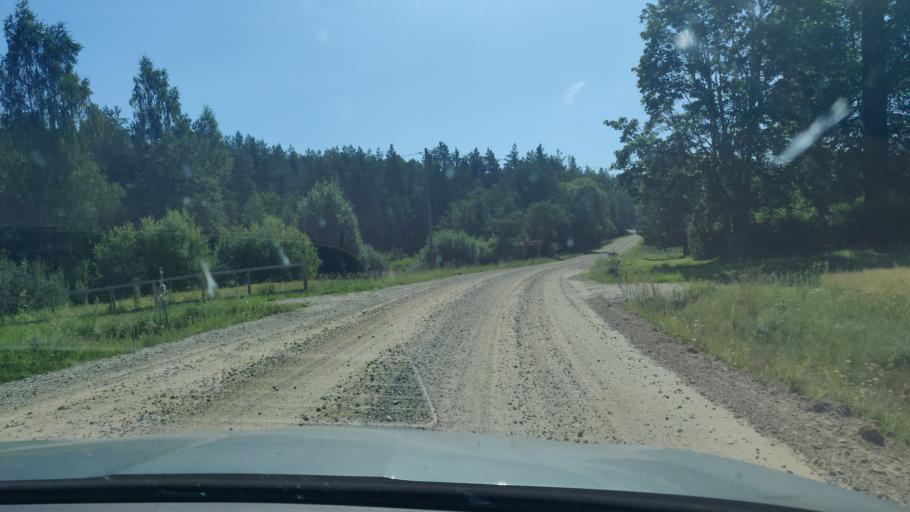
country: EE
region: Tartu
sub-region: Elva linn
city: Elva
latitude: 58.1332
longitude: 26.4089
